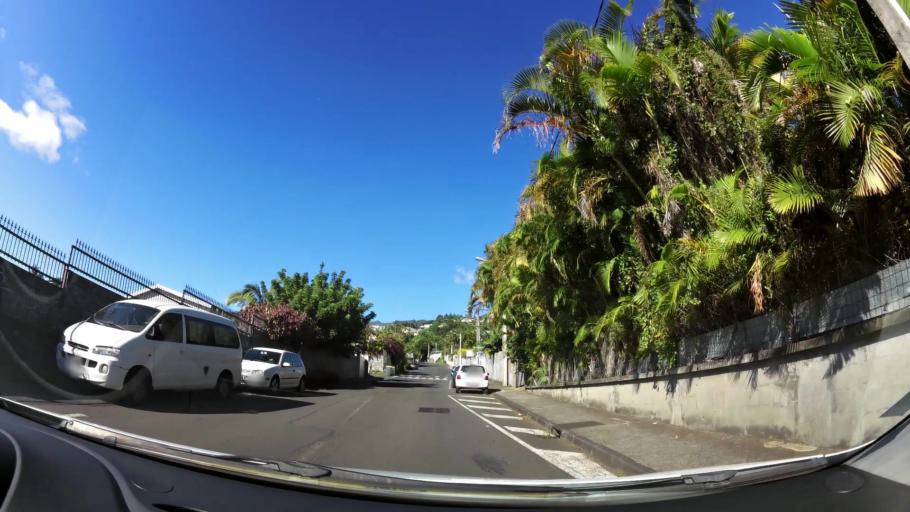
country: RE
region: Reunion
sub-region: Reunion
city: Saint-Denis
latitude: -20.9235
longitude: 55.4736
